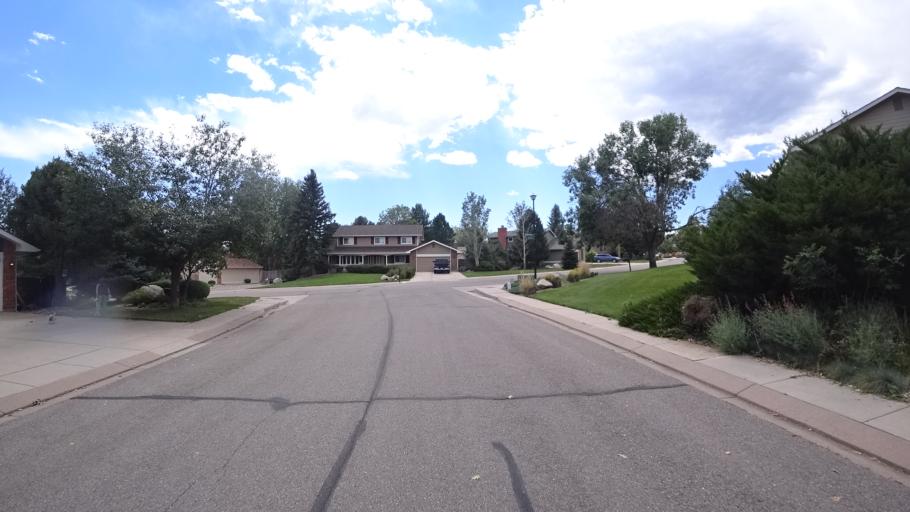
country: US
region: Colorado
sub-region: El Paso County
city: Stratmoor
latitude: 38.7725
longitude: -104.8175
